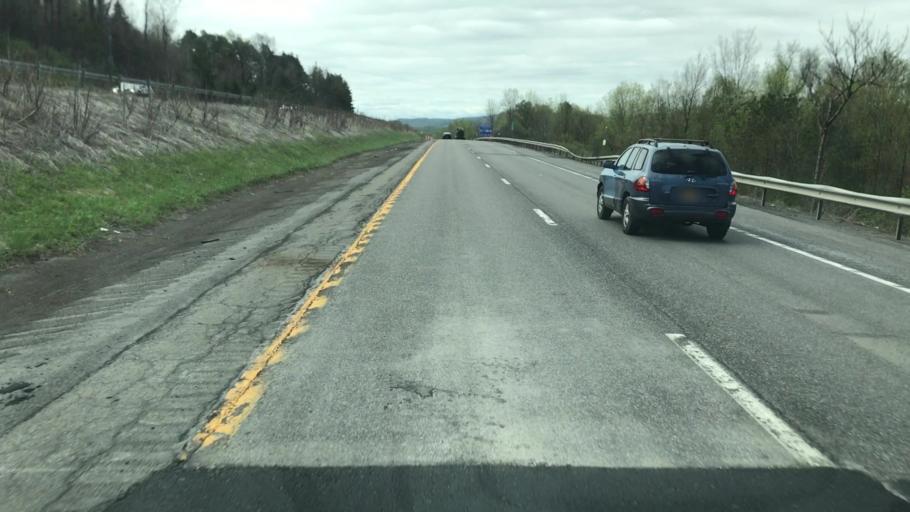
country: US
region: New York
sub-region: Onondaga County
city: Nedrow
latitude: 42.8462
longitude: -76.1218
